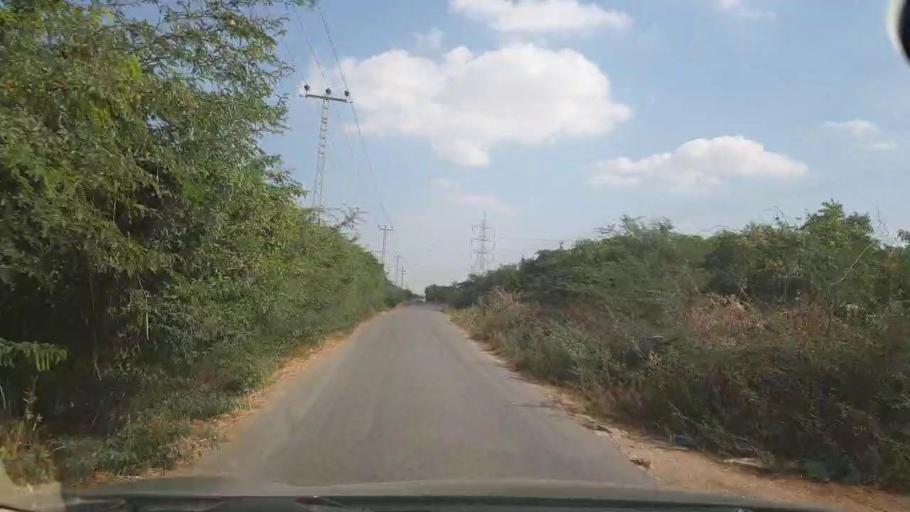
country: PK
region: Sindh
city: Malir Cantonment
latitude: 25.0192
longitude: 67.3632
